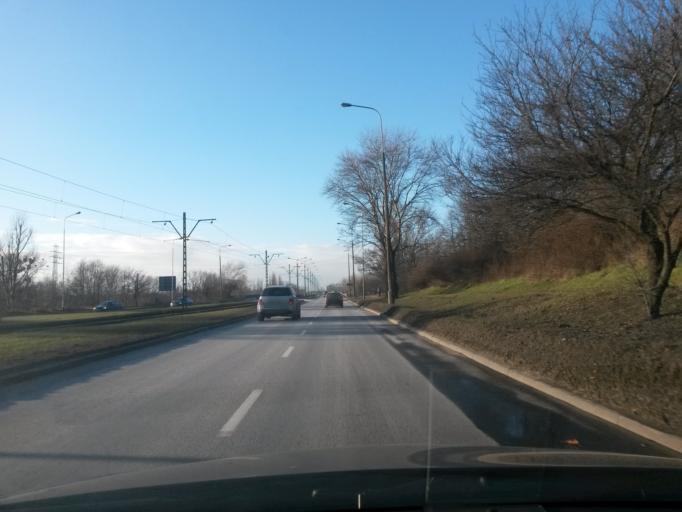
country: PL
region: Greater Poland Voivodeship
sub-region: Poznan
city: Poznan
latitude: 52.3814
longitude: 16.9396
